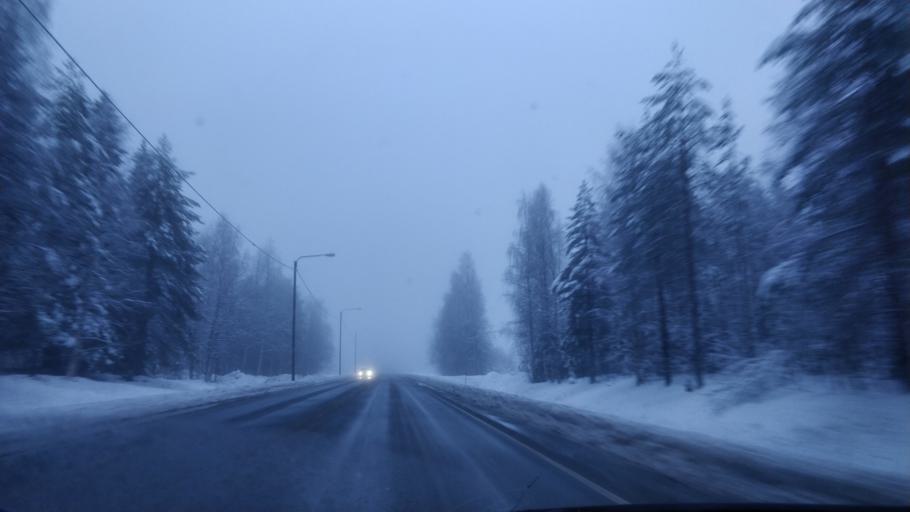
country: FI
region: Lapland
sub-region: Kemi-Tornio
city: Tervola
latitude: 66.1337
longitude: 24.9133
